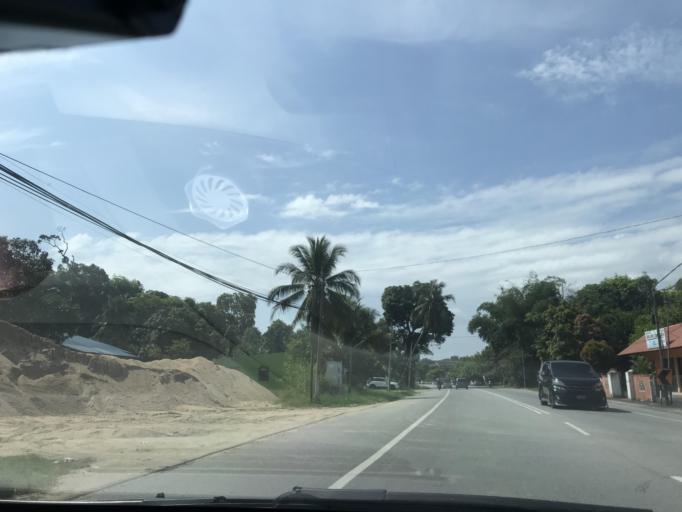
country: MY
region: Kelantan
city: Tumpat
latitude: 6.1399
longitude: 102.1690
